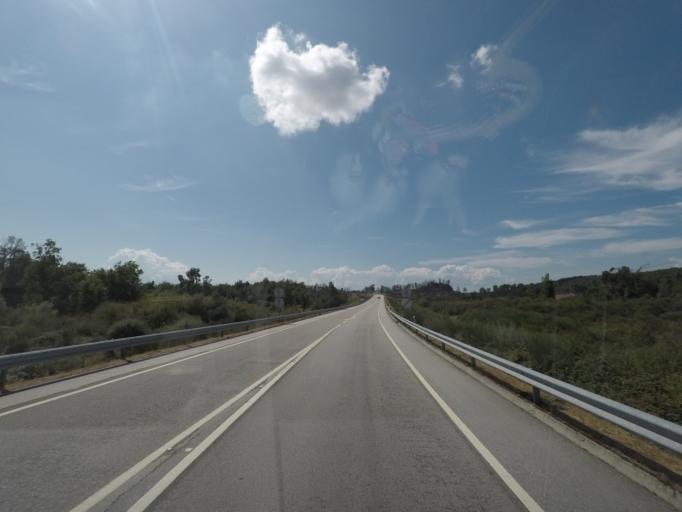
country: PT
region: Vila Real
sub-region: Murca
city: Murca
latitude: 41.3337
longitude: -7.4701
